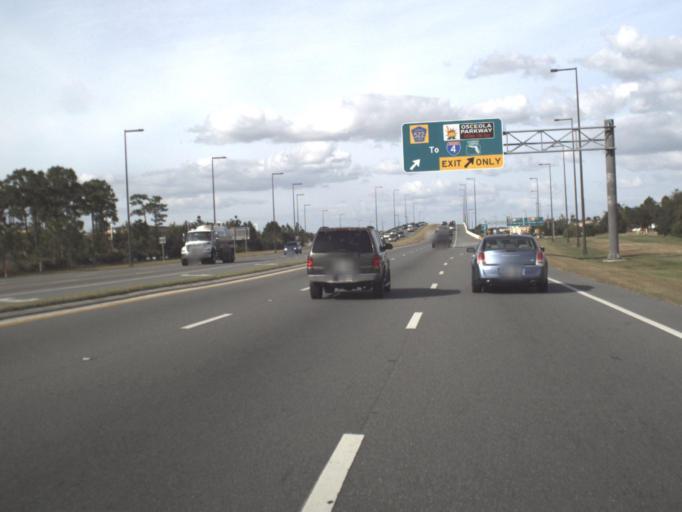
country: US
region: Florida
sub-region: Orange County
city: Hunters Creek
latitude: 28.3378
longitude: -81.4196
